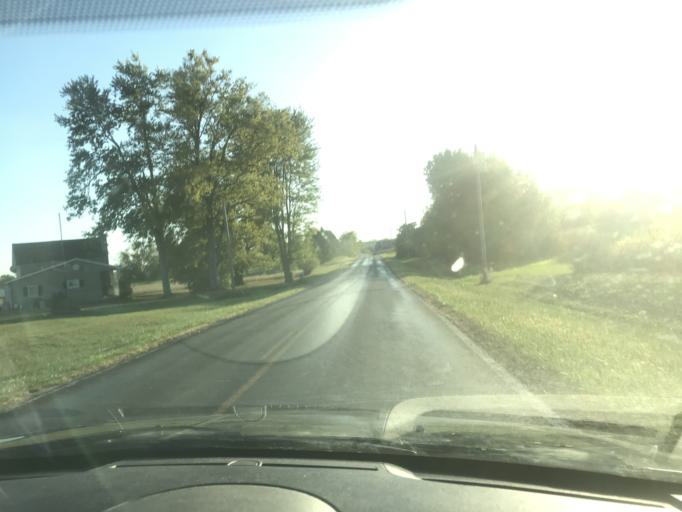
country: US
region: Ohio
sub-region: Logan County
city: De Graff
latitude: 40.2630
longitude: -83.8605
